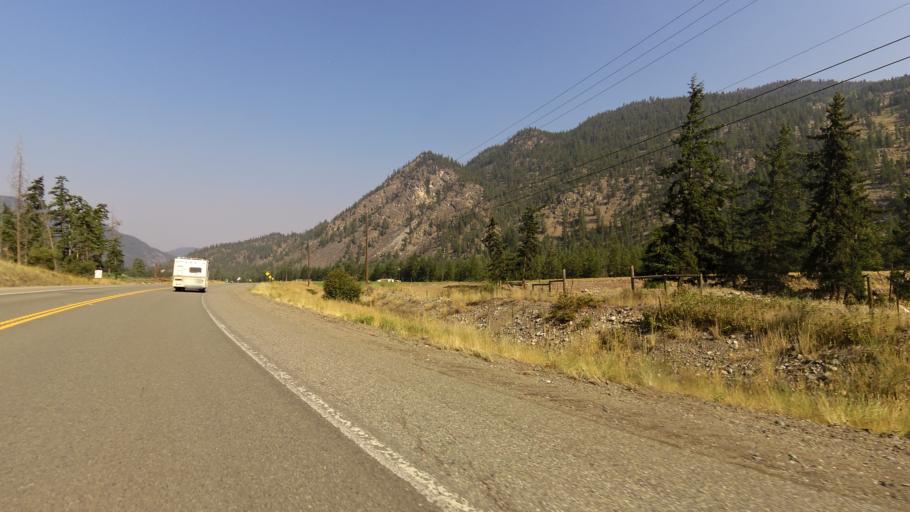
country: CA
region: British Columbia
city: Princeton
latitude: 49.3777
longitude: -120.1564
